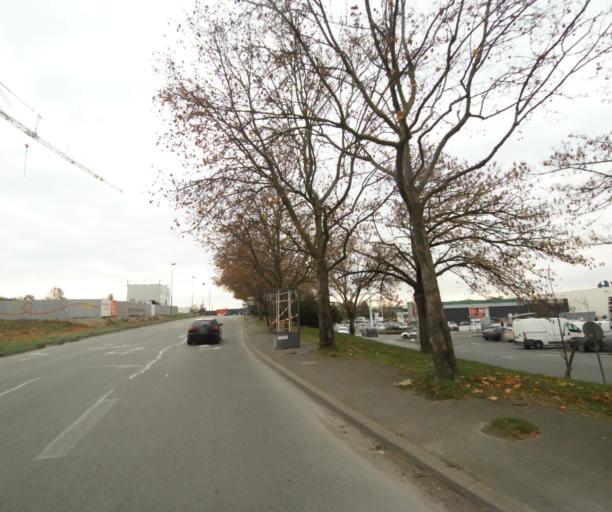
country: FR
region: Ile-de-France
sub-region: Departement de Seine-Saint-Denis
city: Aulnay-sous-Bois
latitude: 48.9570
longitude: 2.4791
